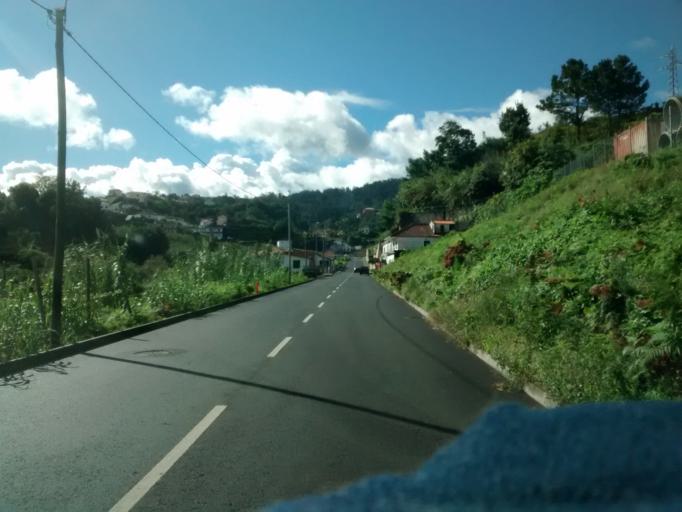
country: PT
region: Madeira
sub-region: Santana
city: Santana
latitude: 32.8088
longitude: -16.8845
